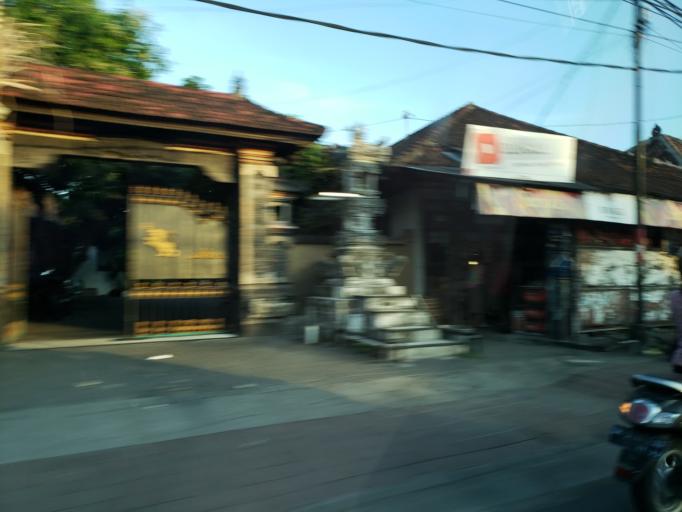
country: ID
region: Bali
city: Kelanabian
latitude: -8.7623
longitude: 115.1789
